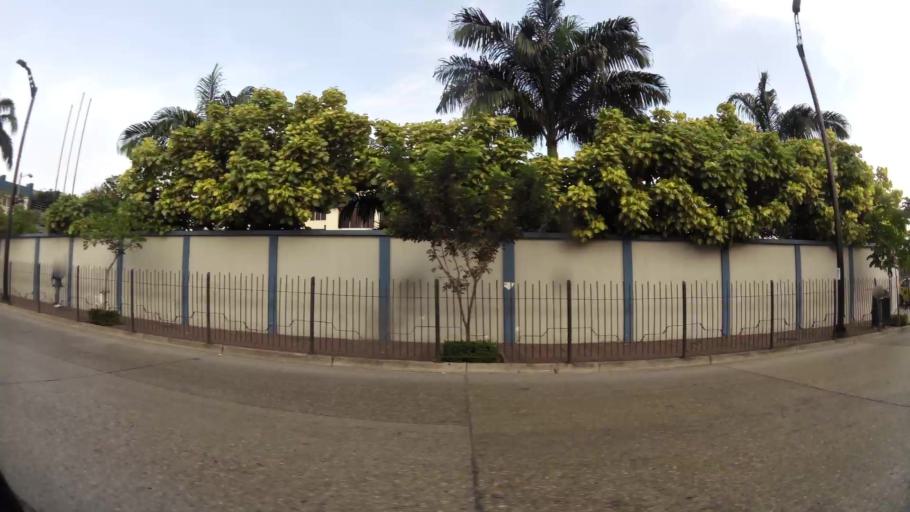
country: EC
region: Guayas
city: Guayaquil
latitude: -2.1754
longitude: -79.8920
